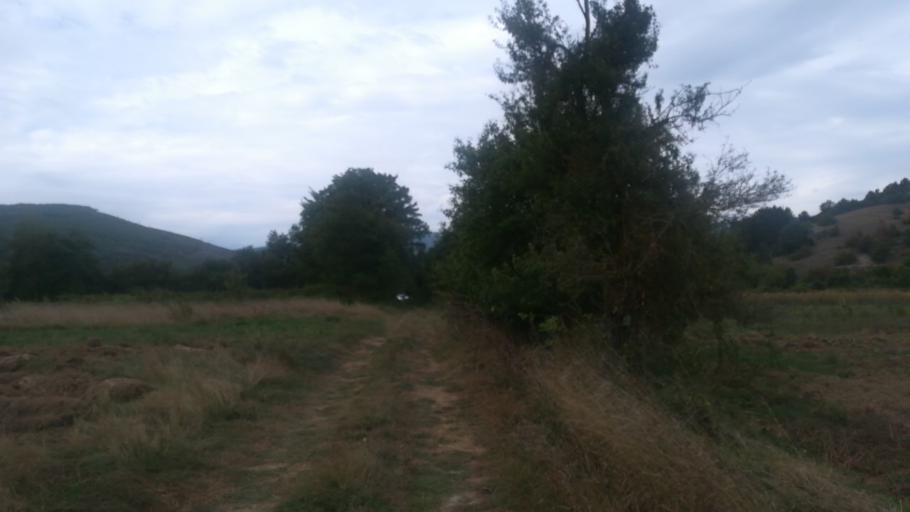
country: MK
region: Debarca
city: Belcista
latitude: 41.2852
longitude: 20.8315
